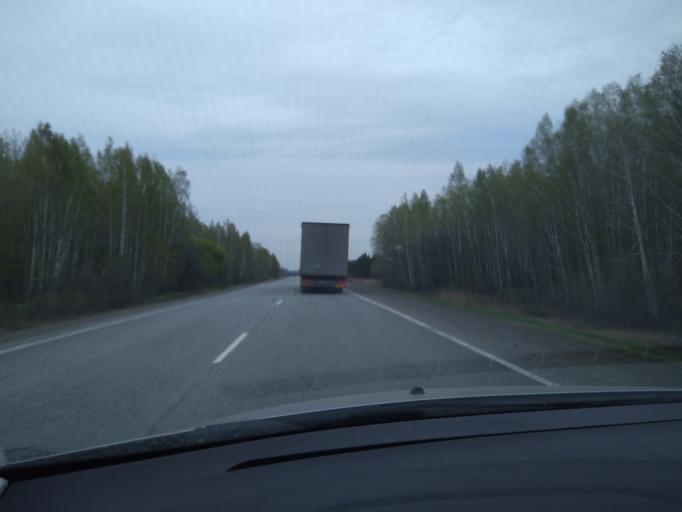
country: RU
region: Sverdlovsk
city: Yelanskiy
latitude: 56.7679
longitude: 62.4306
